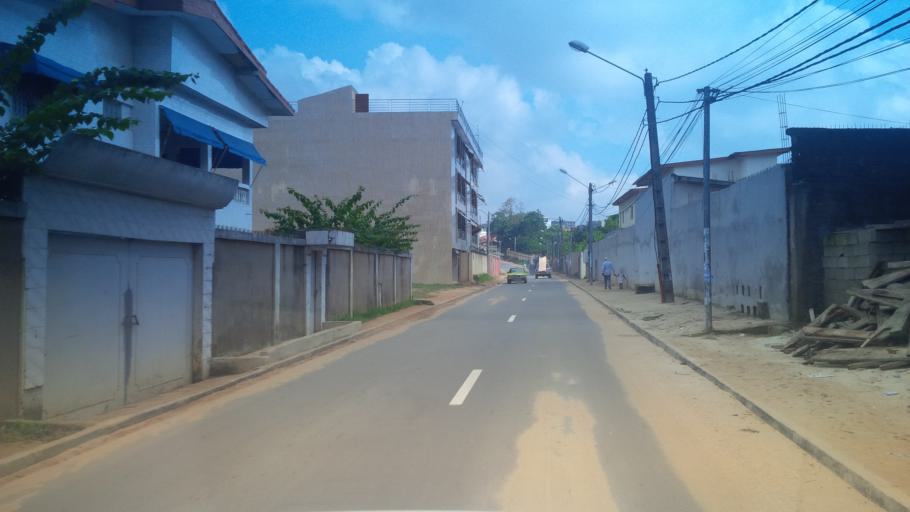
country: CI
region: Lagunes
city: Abobo
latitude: 5.3799
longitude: -3.9536
